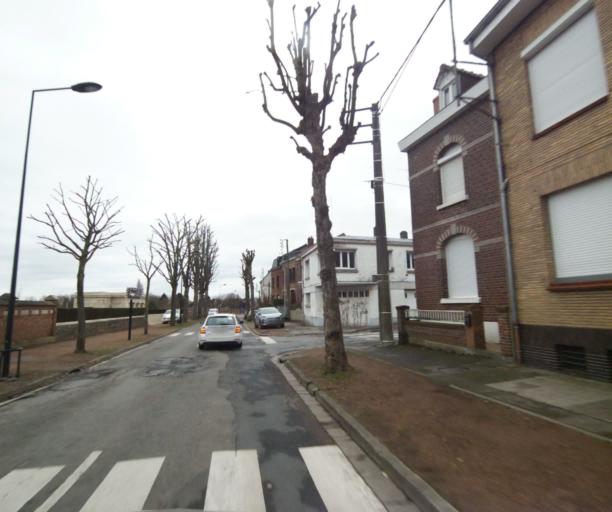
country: FR
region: Nord-Pas-de-Calais
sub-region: Departement du Nord
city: Valenciennes
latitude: 50.3667
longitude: 3.5386
